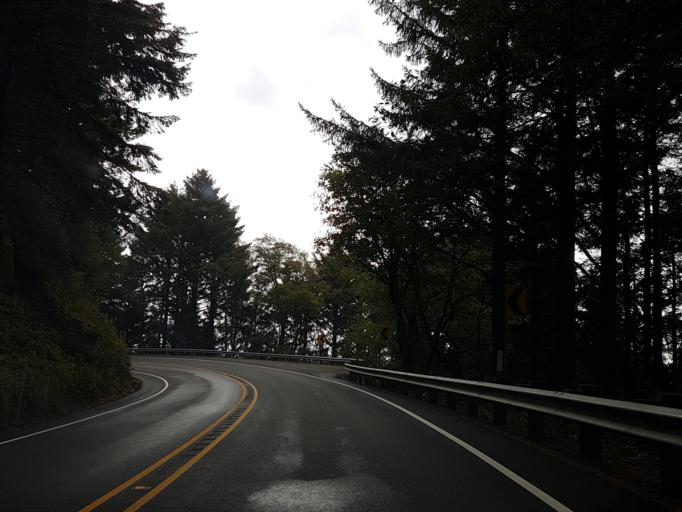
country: US
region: Oregon
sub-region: Lane County
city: Florence
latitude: 44.1159
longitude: -124.1219
